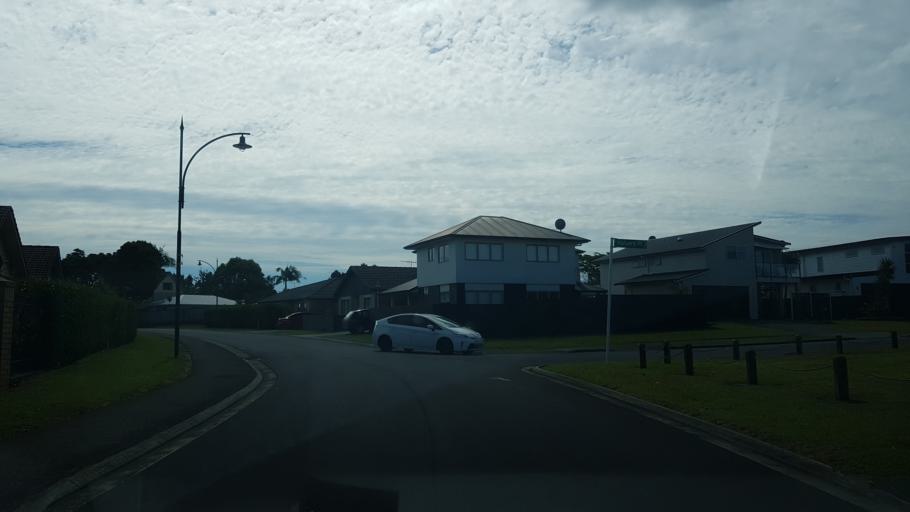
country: NZ
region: Auckland
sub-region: Auckland
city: Rosebank
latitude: -36.8346
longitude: 174.6583
